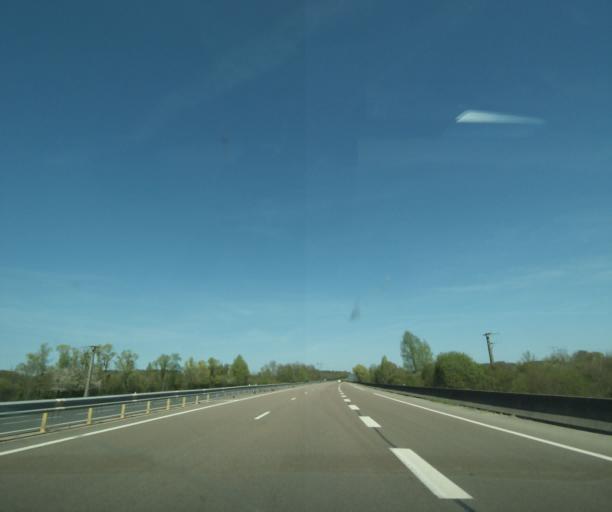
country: FR
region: Bourgogne
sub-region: Departement de la Nievre
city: Garchizy
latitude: 47.0524
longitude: 3.1313
